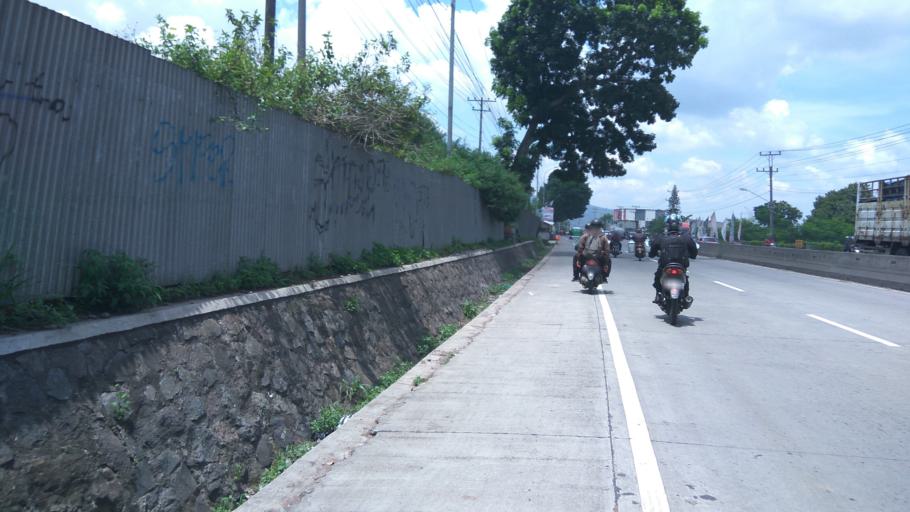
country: ID
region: Central Java
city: Ungaran
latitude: -7.1804
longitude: 110.4232
